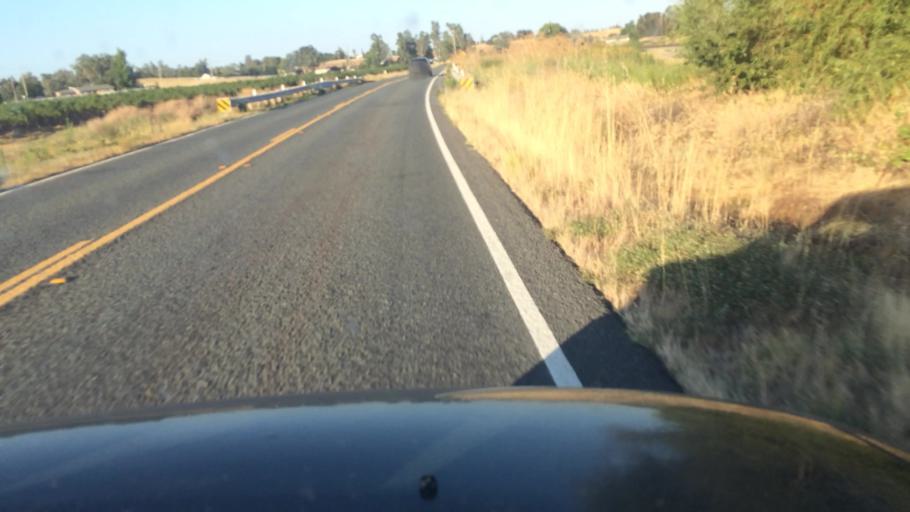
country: US
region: California
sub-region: Sacramento County
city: Clay
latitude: 38.3392
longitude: -121.1545
